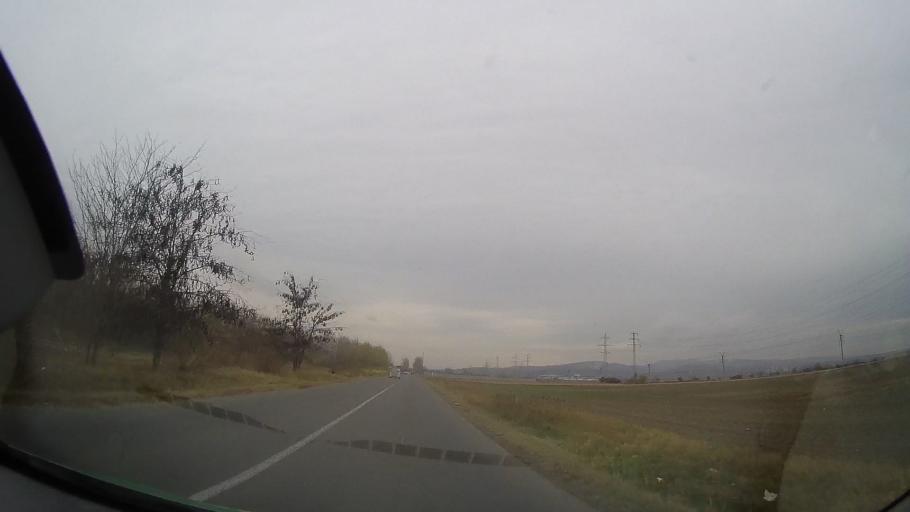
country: RO
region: Prahova
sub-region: Oras Urlati
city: Urlati
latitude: 44.9656
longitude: 26.2346
